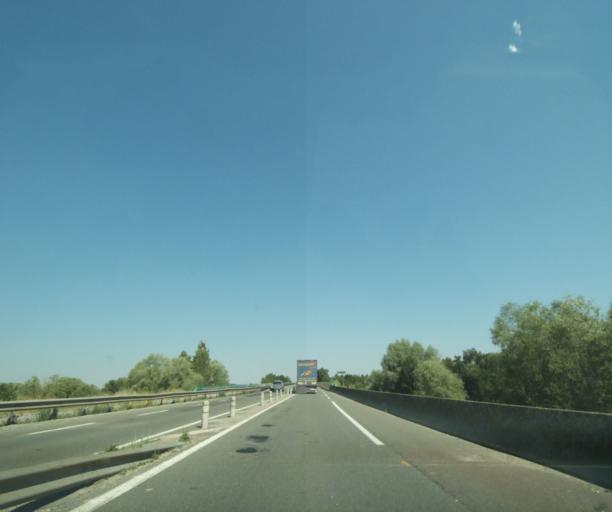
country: FR
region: Champagne-Ardenne
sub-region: Departement de la Haute-Marne
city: Saint-Dizier
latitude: 48.6325
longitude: 4.9254
